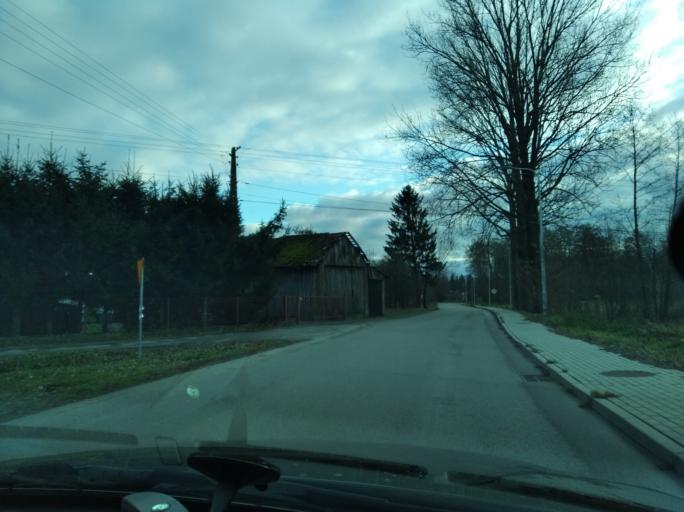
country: PL
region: Subcarpathian Voivodeship
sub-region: Powiat rzeszowski
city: Krasne
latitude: 50.0731
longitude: 22.1124
